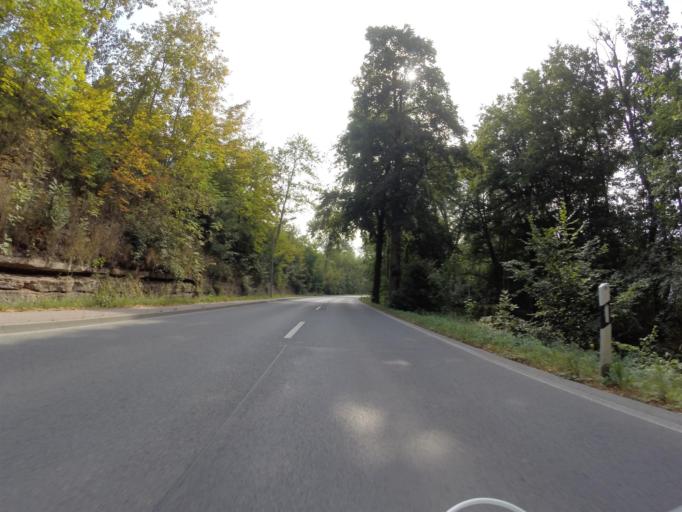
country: DE
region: Thuringia
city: Stadtroda
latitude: 50.8671
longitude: 11.7220
